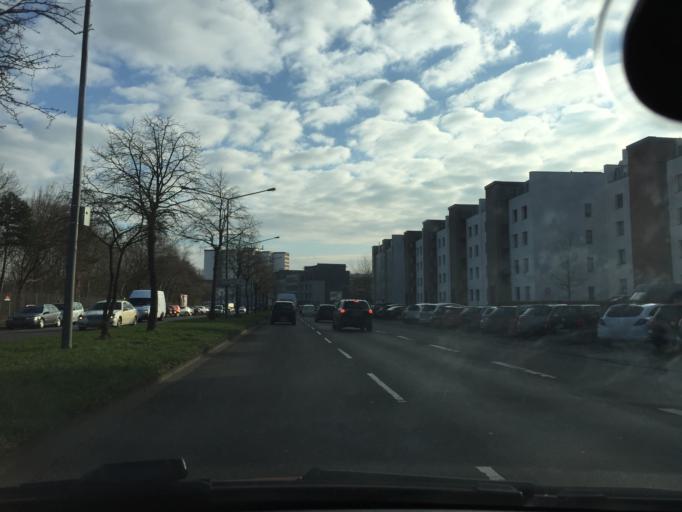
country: DE
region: North Rhine-Westphalia
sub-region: Regierungsbezirk Koln
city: Neustadt/Sued
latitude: 50.9164
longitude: 6.9427
